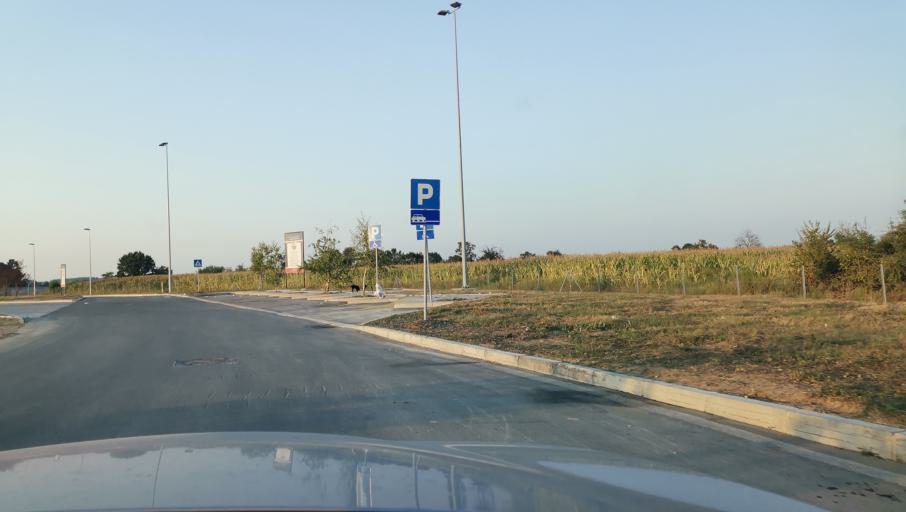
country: RS
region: Central Serbia
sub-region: Kolubarski Okrug
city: Ub
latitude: 44.4056
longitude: 20.0952
